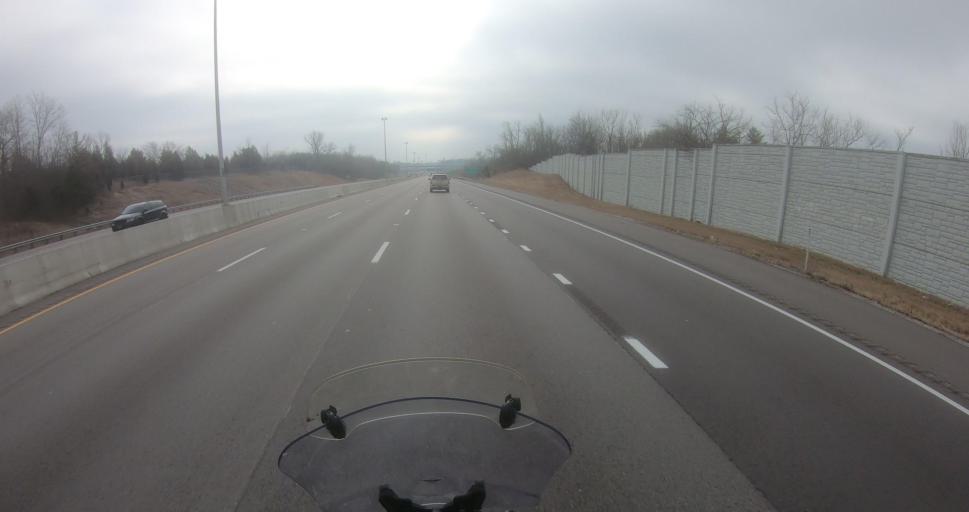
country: US
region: Ohio
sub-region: Montgomery County
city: Vandalia
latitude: 39.8762
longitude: -84.1880
